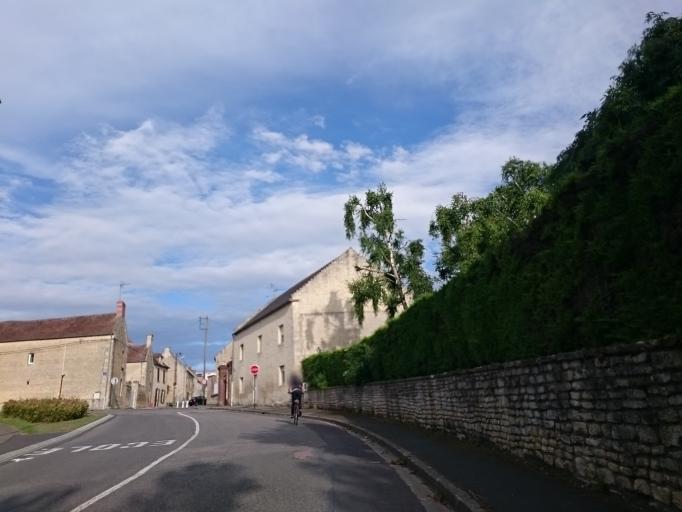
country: FR
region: Lower Normandy
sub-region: Departement du Calvados
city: Fleury-sur-Orne
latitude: 49.1424
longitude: -0.3846
